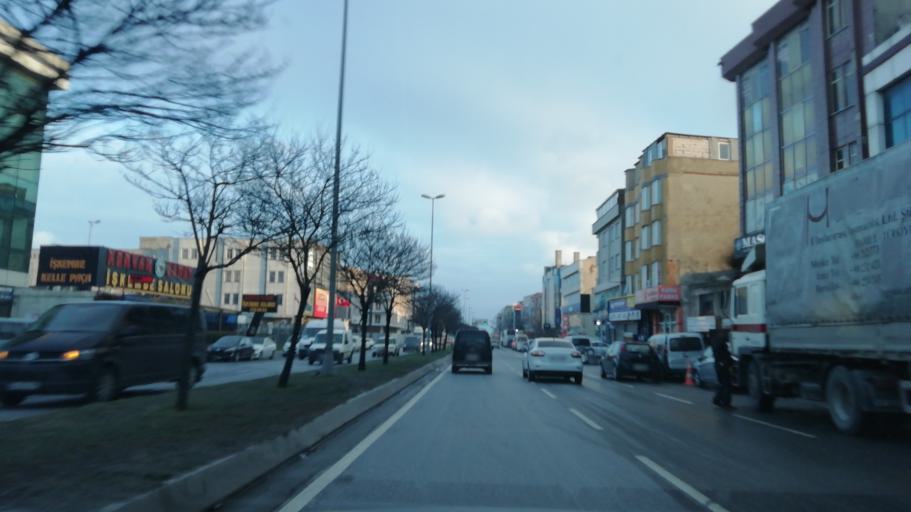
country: TR
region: Istanbul
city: Esenyurt
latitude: 41.0090
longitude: 28.7024
